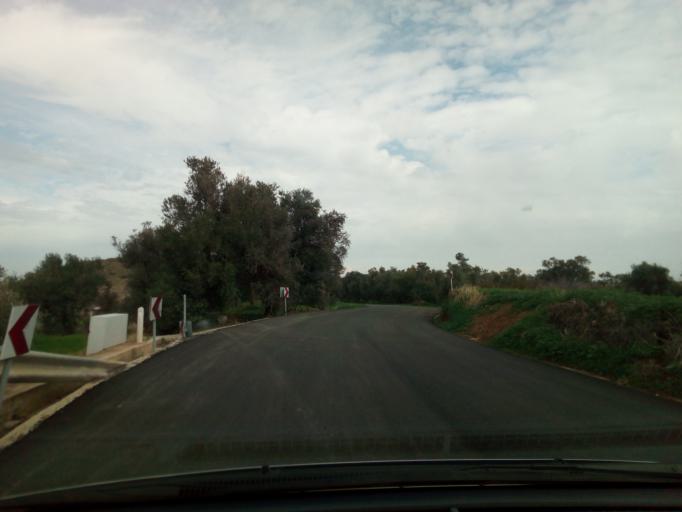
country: CY
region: Lefkosia
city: Astromeritis
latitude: 35.0786
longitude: 32.9953
